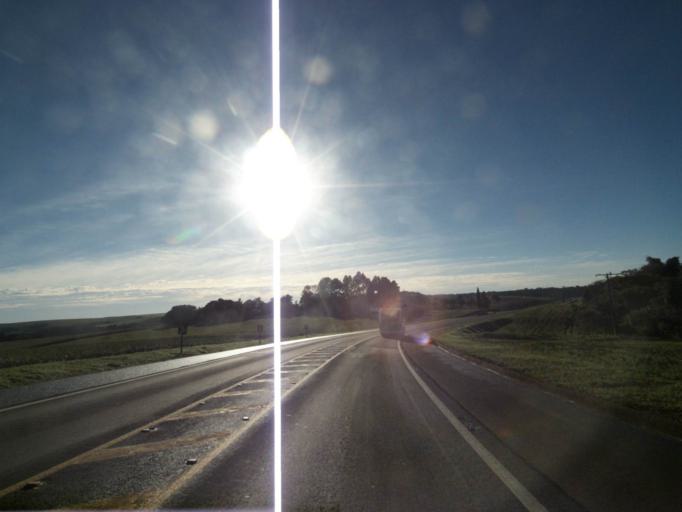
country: BR
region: Parana
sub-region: Matelandia
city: Matelandia
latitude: -25.1075
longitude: -53.7622
